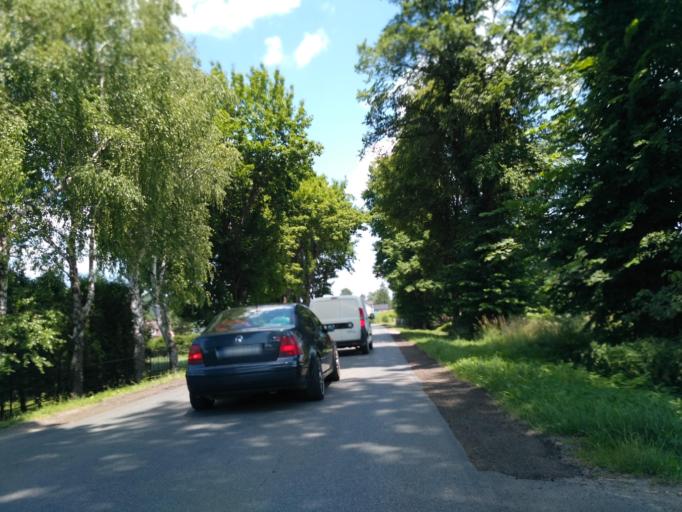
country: PL
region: Subcarpathian Voivodeship
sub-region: Powiat sanocki
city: Niebieszczany
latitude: 49.5408
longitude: 22.1321
